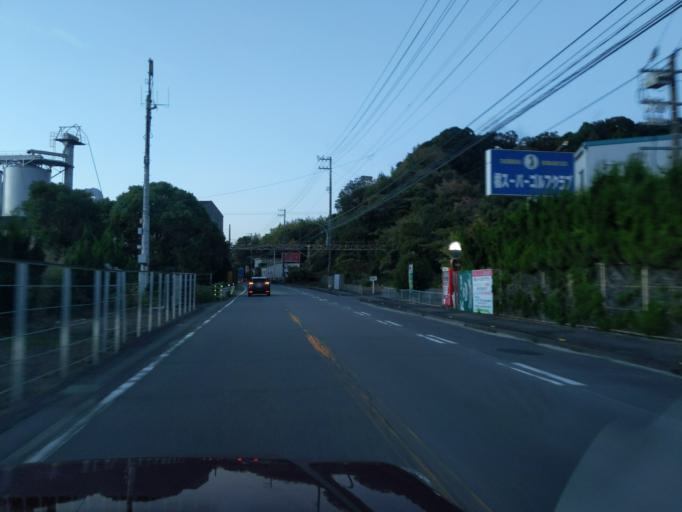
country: JP
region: Tokushima
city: Anan
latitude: 33.8687
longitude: 134.6331
